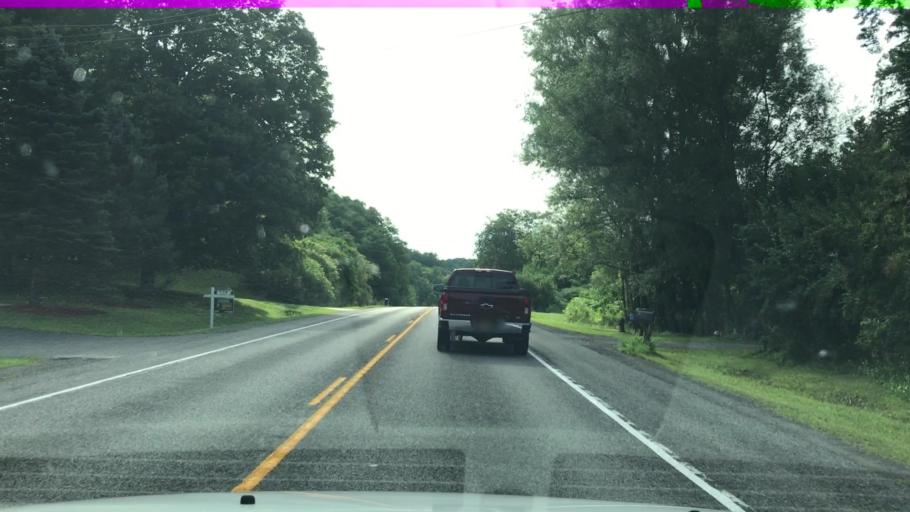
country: US
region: New York
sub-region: Erie County
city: Alden
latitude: 42.8475
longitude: -78.4783
